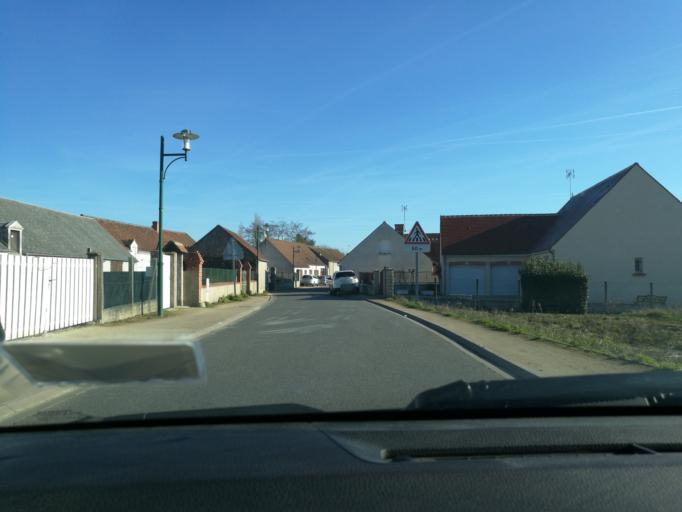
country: FR
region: Centre
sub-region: Departement du Loiret
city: Chaingy
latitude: 47.8764
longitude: 1.7681
